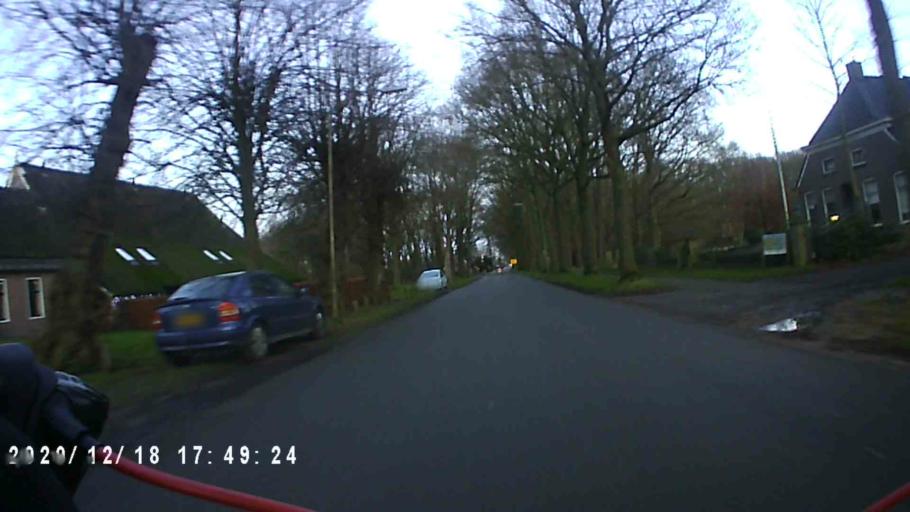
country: NL
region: Drenthe
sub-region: Gemeente Tynaarlo
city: Vries
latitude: 53.1128
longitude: 6.5871
